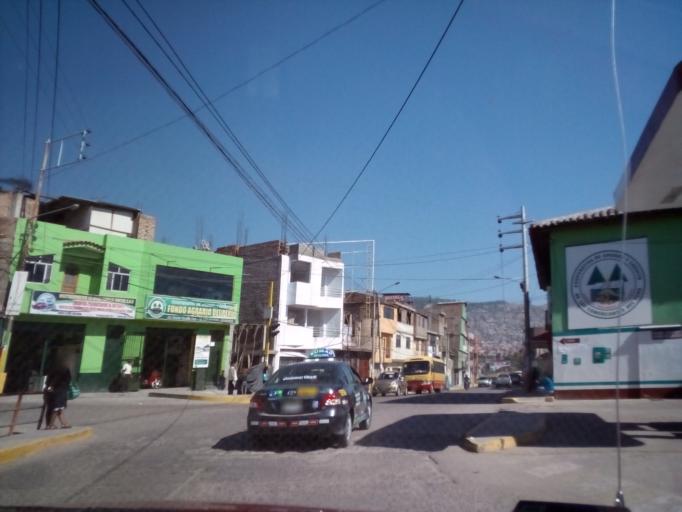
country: PE
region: Ayacucho
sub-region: Provincia de Huamanga
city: Ayacucho
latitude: -13.1659
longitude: -74.2156
